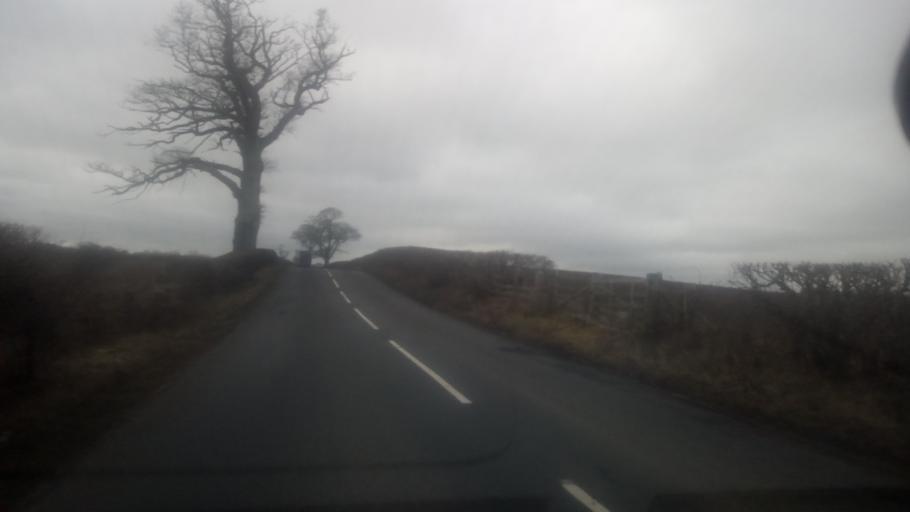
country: GB
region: Scotland
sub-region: The Scottish Borders
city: Kelso
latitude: 55.5890
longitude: -2.4815
